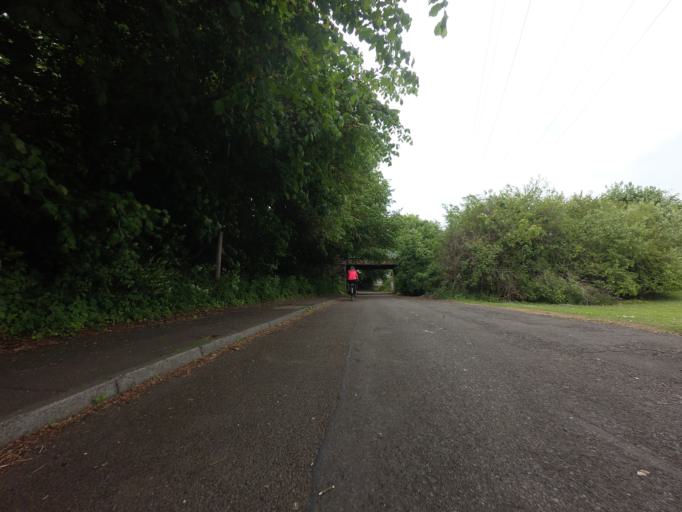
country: GB
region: Scotland
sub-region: Fife
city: Townhill
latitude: 56.0790
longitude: -3.4233
